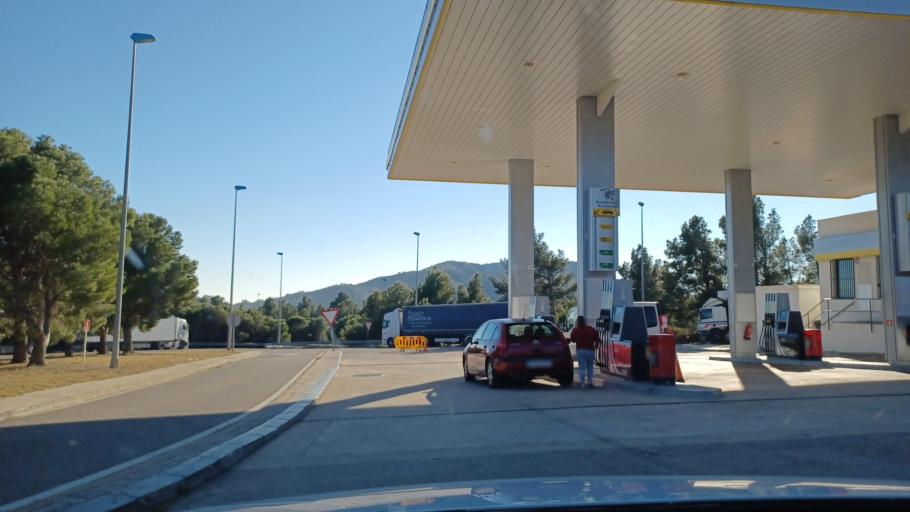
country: ES
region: Catalonia
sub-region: Provincia de Tarragona
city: Colldejou
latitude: 40.9859
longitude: 0.8940
